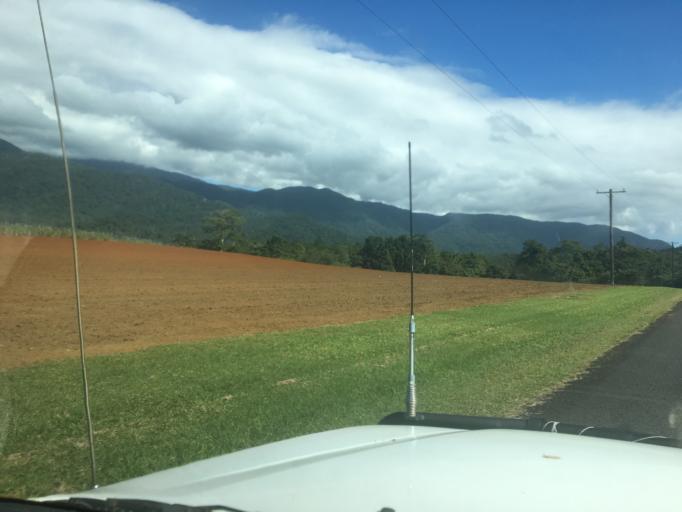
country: AU
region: Queensland
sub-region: Cassowary Coast
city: Innisfail
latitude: -17.3478
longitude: 145.8901
